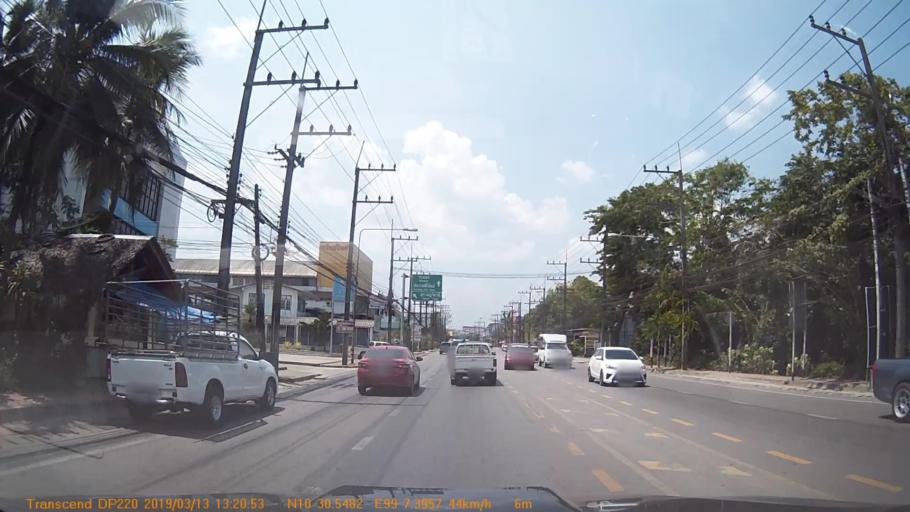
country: TH
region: Chumphon
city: Chumphon
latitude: 10.5083
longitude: 99.1246
